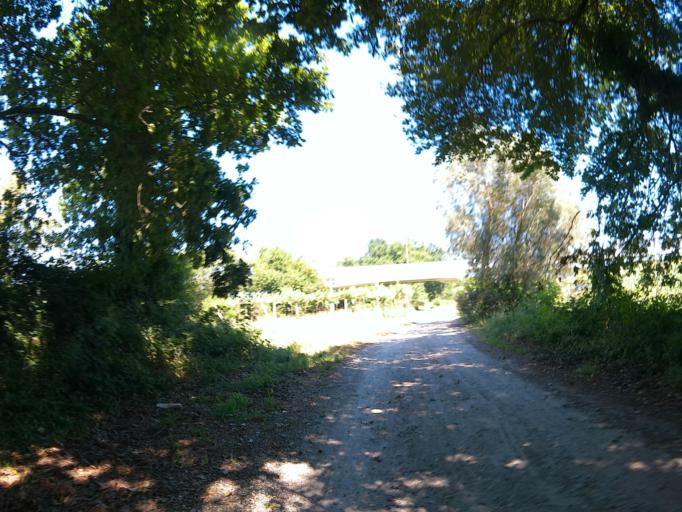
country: PT
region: Viana do Castelo
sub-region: Viana do Castelo
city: Darque
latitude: 41.7234
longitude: -8.6840
